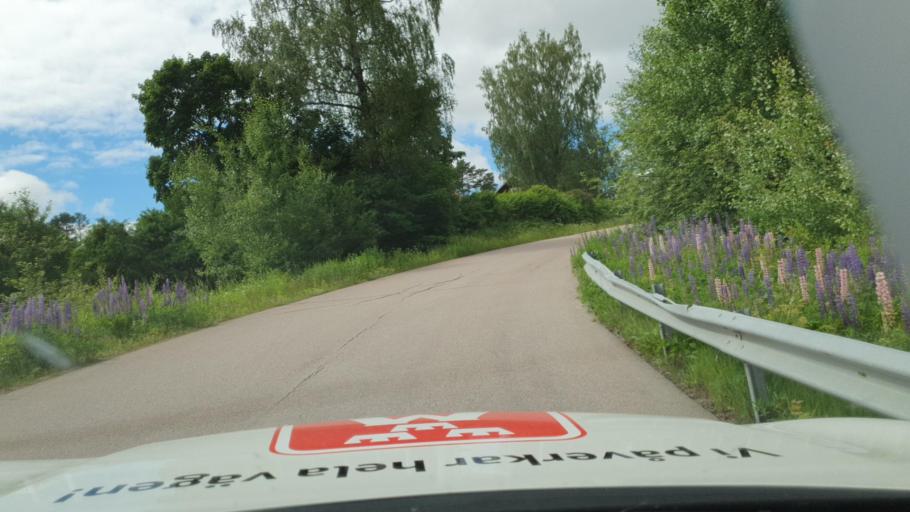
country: SE
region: Vaermland
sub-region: Eda Kommun
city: Charlottenberg
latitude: 59.9199
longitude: 12.2658
